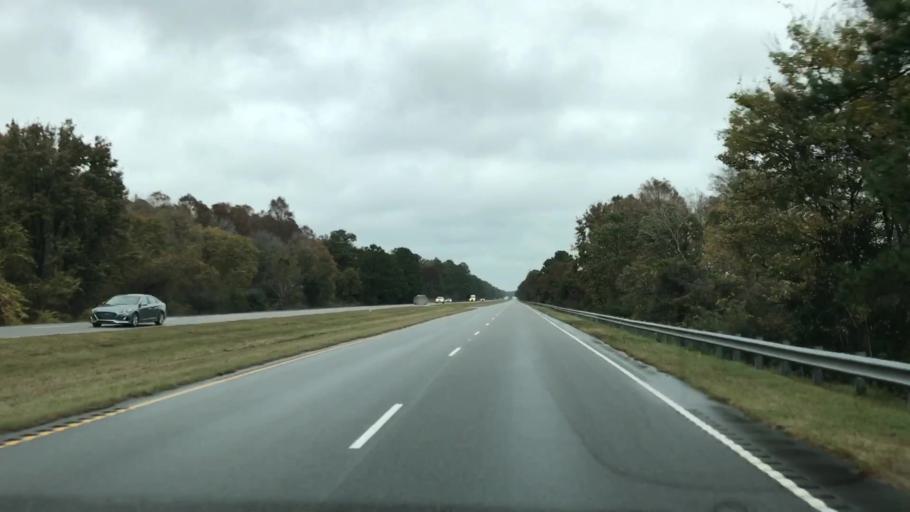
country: US
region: South Carolina
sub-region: Georgetown County
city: Georgetown
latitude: 33.1930
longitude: -79.3980
